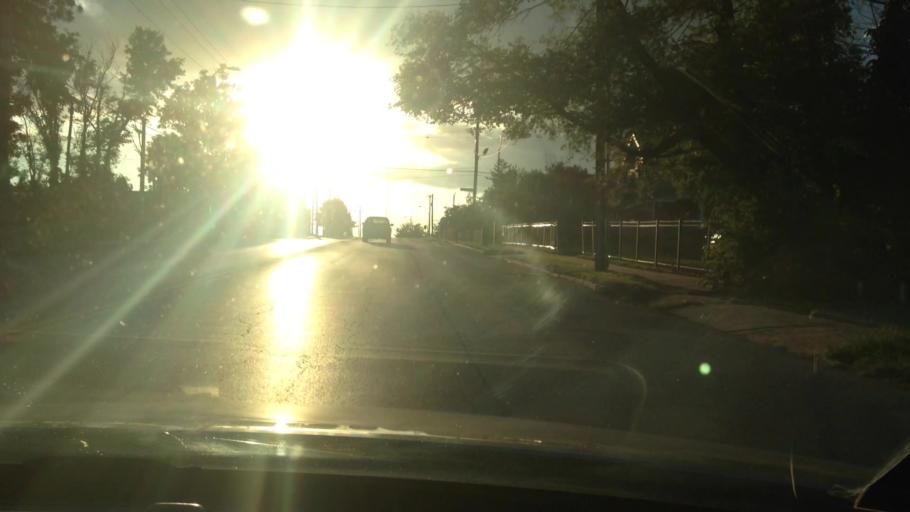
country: US
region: Missouri
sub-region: Jackson County
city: Kansas City
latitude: 39.0698
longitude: -94.5495
